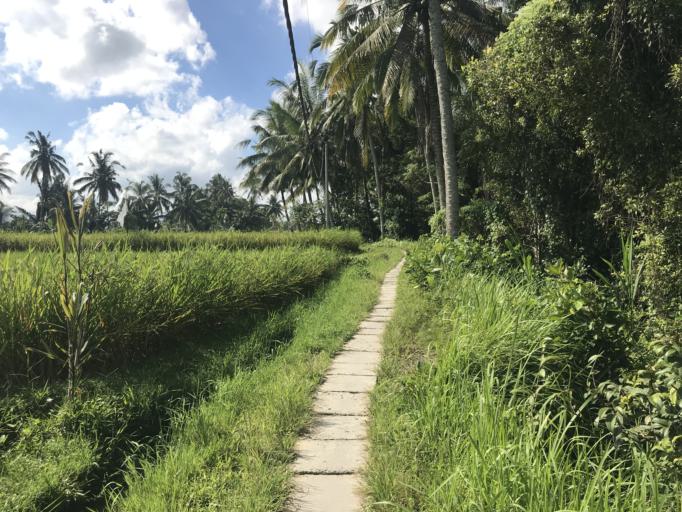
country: ID
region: Bali
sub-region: Kabupaten Gianyar
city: Ubud
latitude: -8.4877
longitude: 115.2616
